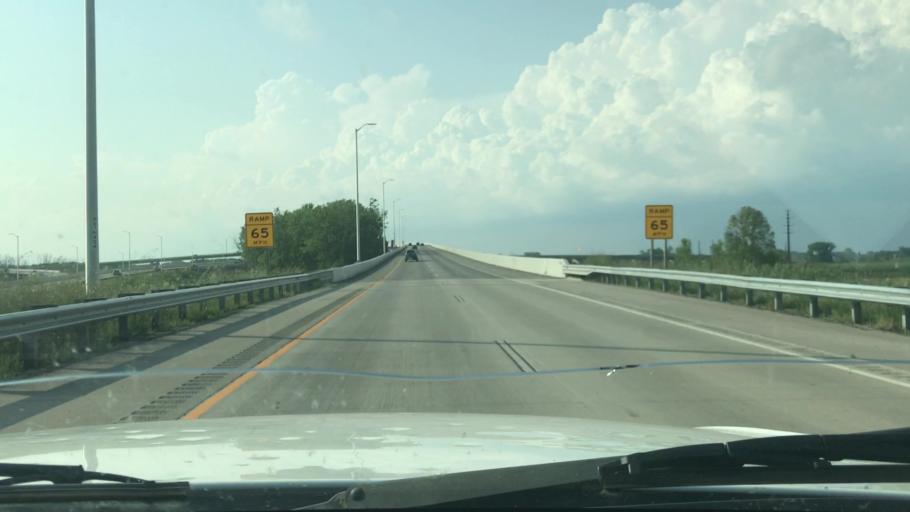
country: US
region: Wisconsin
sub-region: Brown County
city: Howard
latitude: 44.5554
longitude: -88.0457
